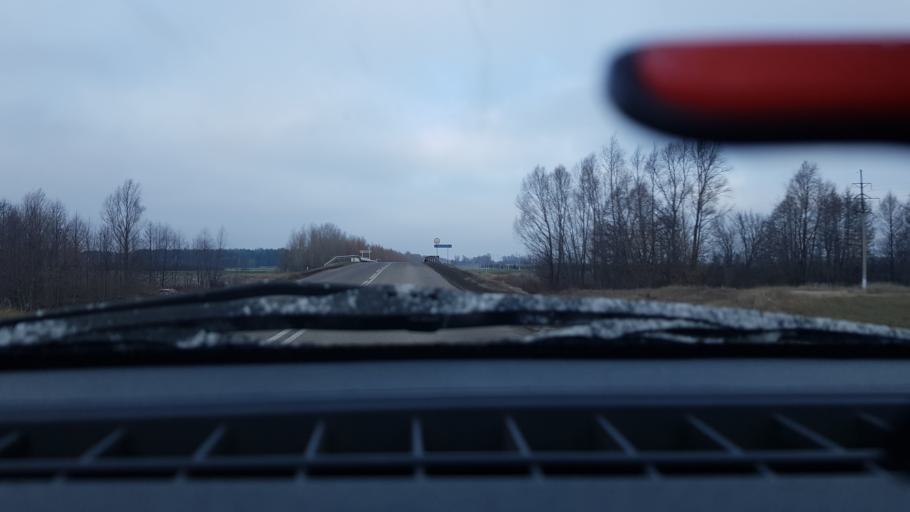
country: RU
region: Tatarstan
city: Kuybyshevskiy Zaton
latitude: 54.9224
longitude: 49.4729
